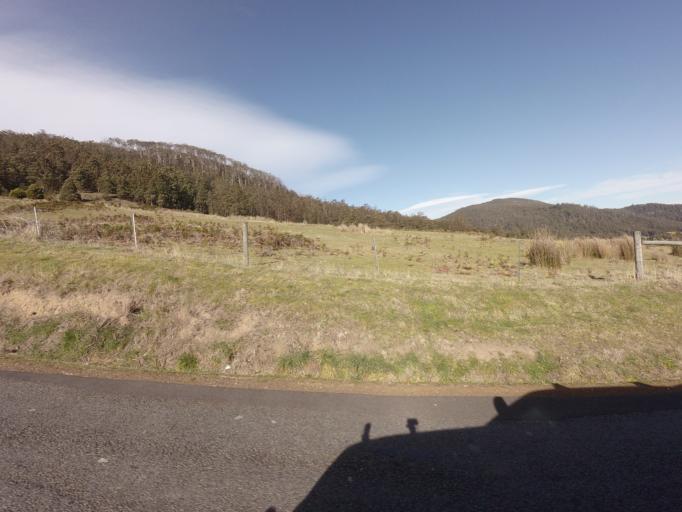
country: AU
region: Tasmania
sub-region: Kingborough
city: Kettering
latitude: -43.1697
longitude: 147.1759
